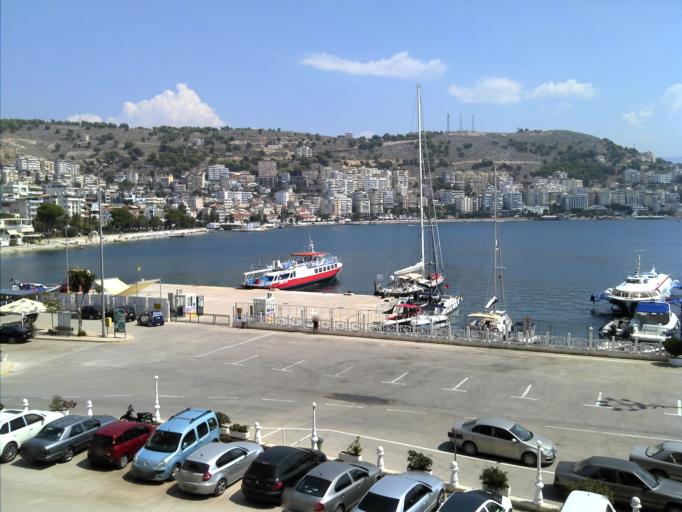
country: AL
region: Vlore
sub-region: Rrethi i Sarandes
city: Sarande
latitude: 39.8708
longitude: 20.0025
